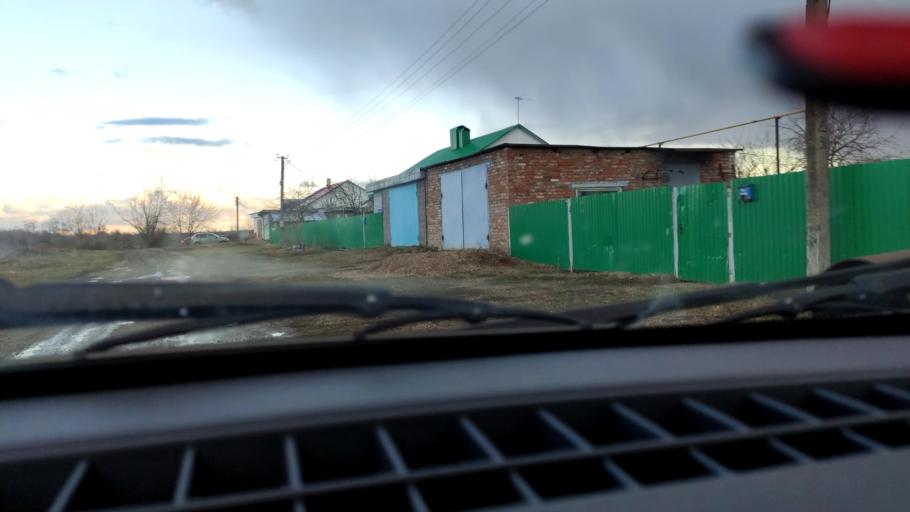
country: RU
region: Bashkortostan
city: Iglino
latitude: 54.7721
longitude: 56.2176
